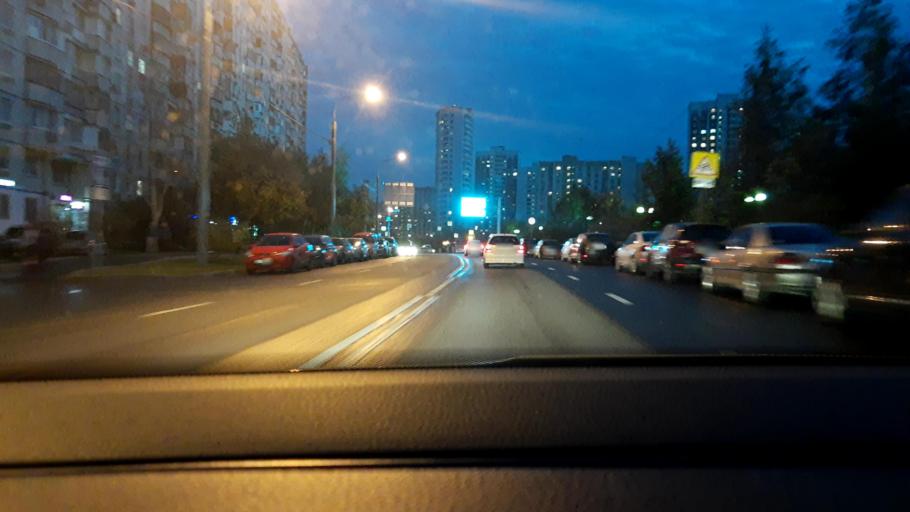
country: RU
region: Moskovskaya
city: Pavshino
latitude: 55.8516
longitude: 37.3539
